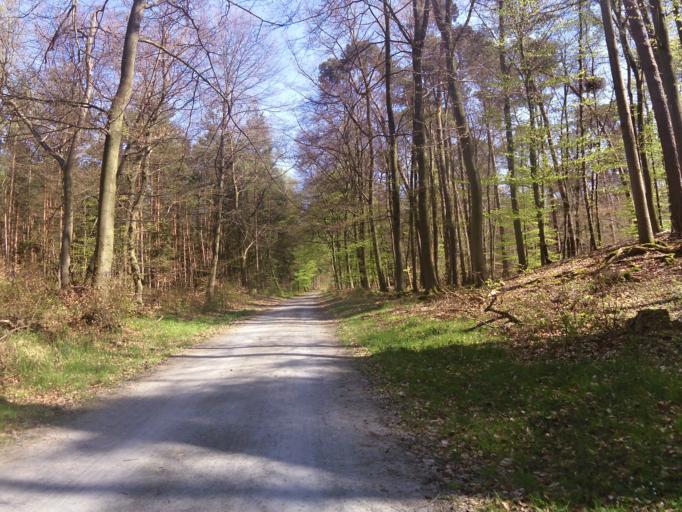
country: DE
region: Hesse
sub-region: Regierungsbezirk Darmstadt
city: Gross-Gerau
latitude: 49.9689
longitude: 8.5247
